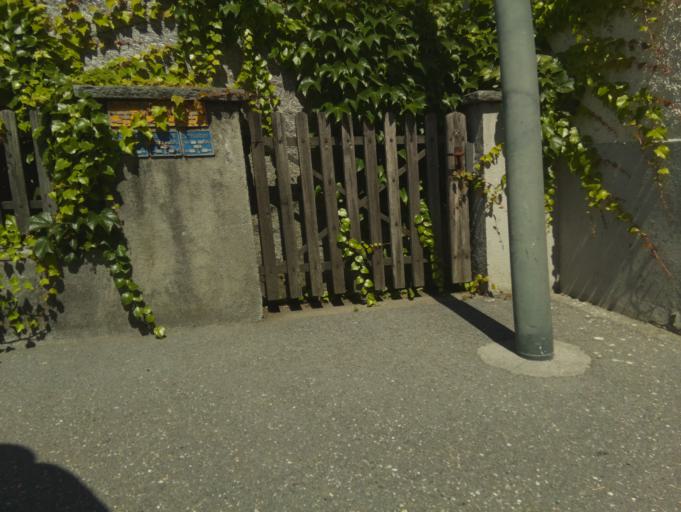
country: CH
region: Glarus
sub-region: Glarus
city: Nafels
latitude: 47.0965
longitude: 9.0625
